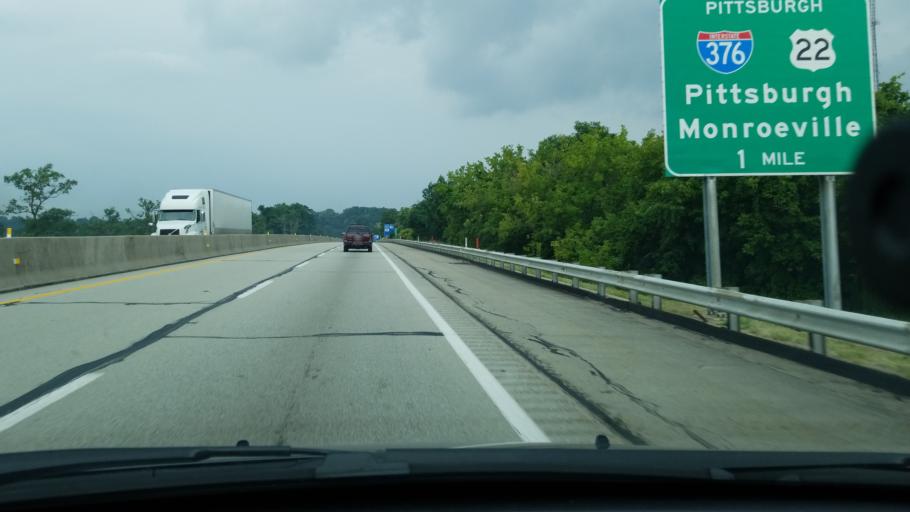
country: US
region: Pennsylvania
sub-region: Allegheny County
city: Monroeville
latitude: 40.4504
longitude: -79.7540
